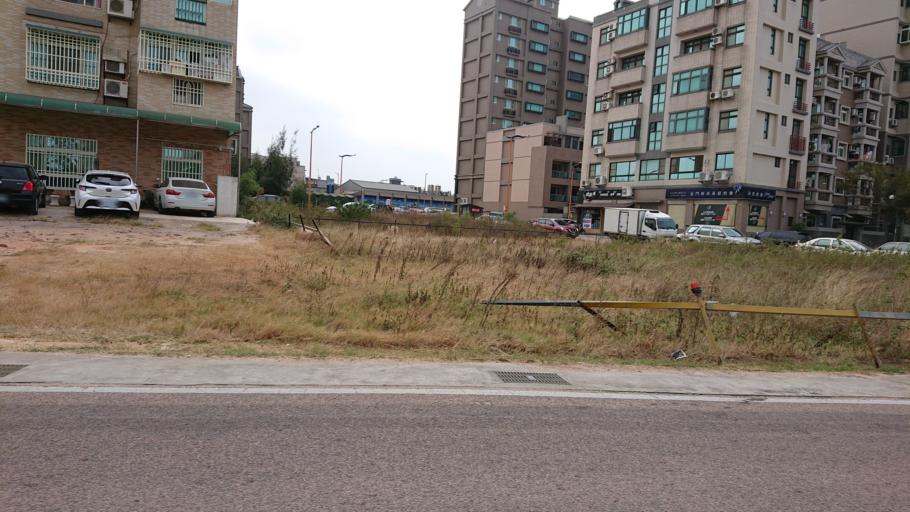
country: TW
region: Fukien
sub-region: Kinmen
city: Jincheng
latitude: 24.4405
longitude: 118.3196
